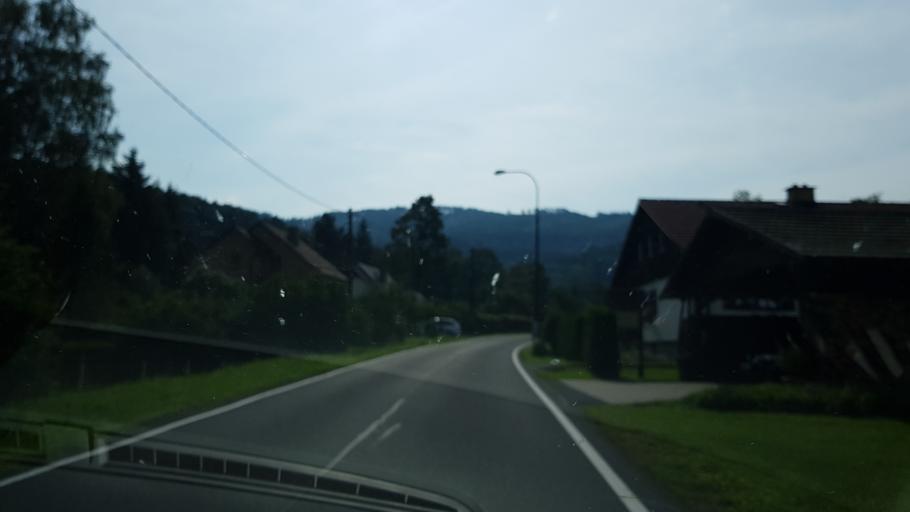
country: CZ
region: Olomoucky
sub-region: Okres Jesenik
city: Jesenik
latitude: 50.2101
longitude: 17.2285
